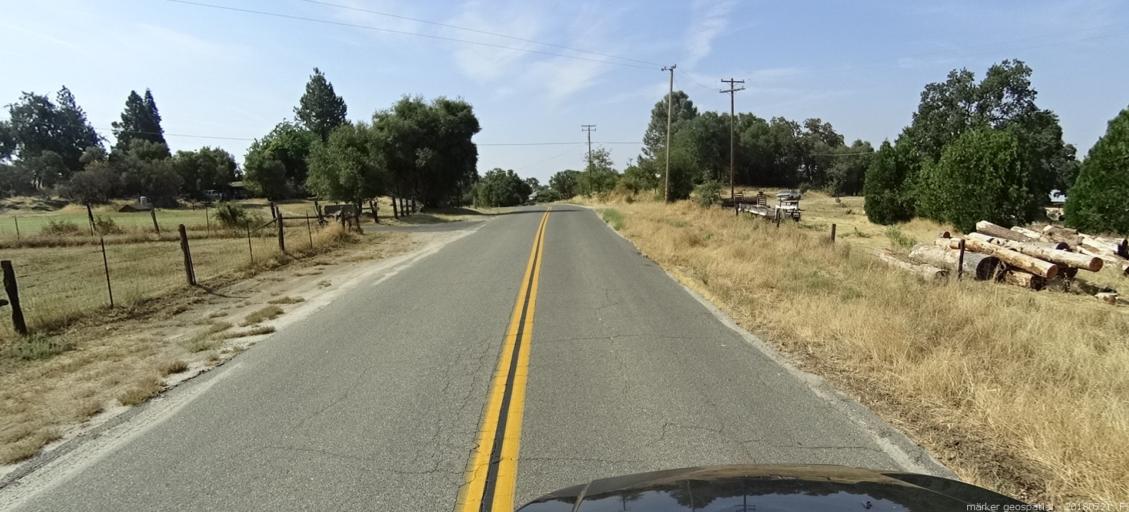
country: US
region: California
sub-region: Fresno County
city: Auberry
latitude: 37.2152
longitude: -119.5291
